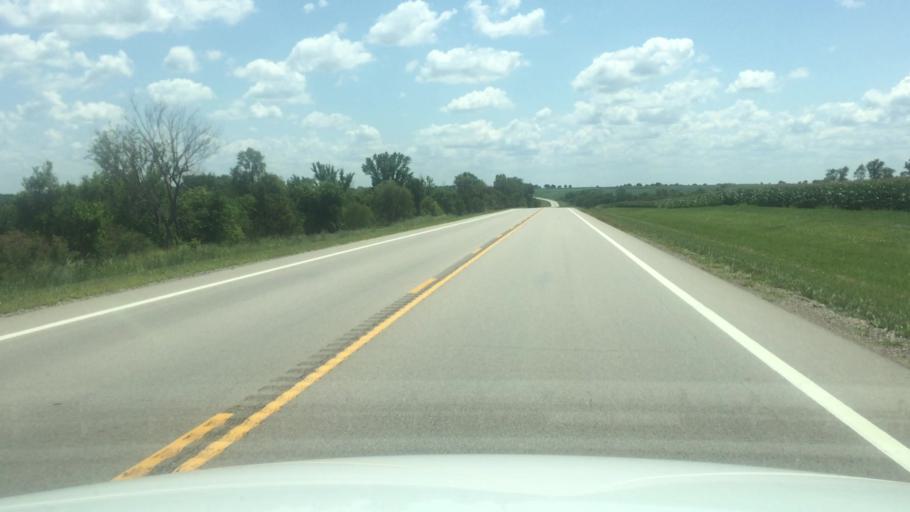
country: US
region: Kansas
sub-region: Brown County
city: Horton
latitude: 39.6295
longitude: -95.3515
